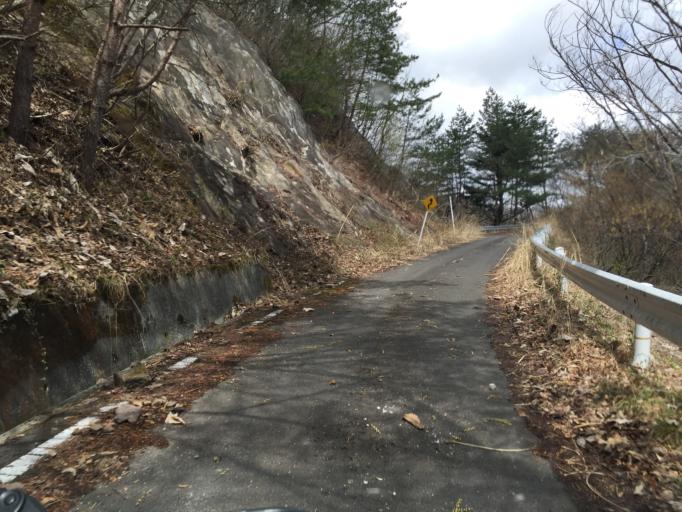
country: JP
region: Fukushima
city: Fukushima-shi
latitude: 37.8566
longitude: 140.4251
